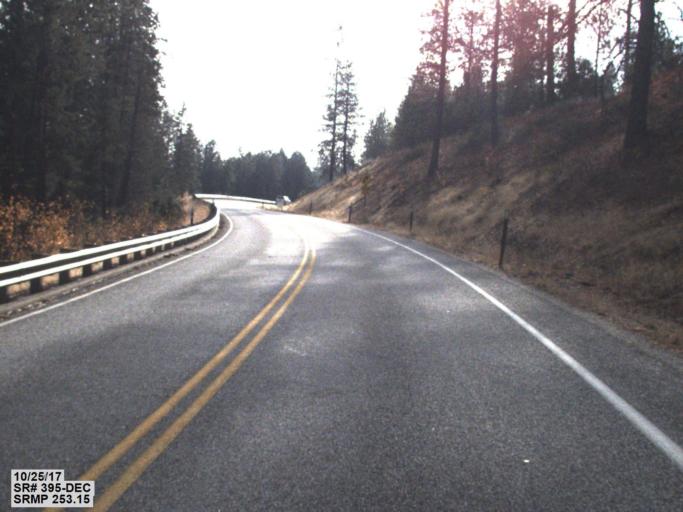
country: US
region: Washington
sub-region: Stevens County
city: Kettle Falls
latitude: 48.7797
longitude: -118.1460
